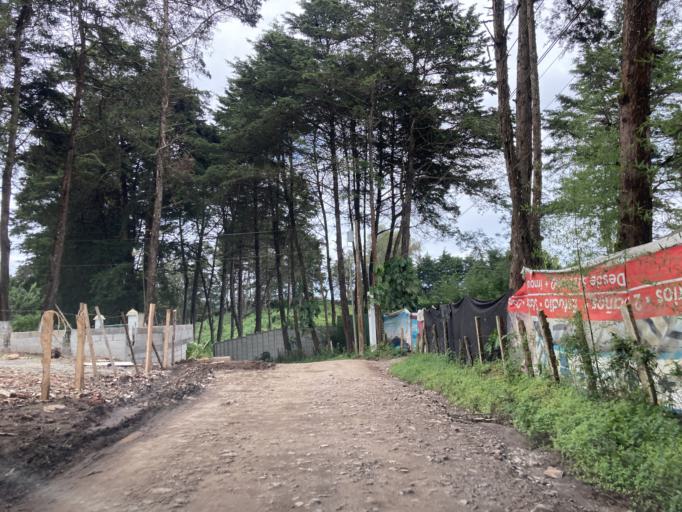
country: GT
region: Guatemala
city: San Jose Pinula
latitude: 14.5341
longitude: -90.4058
